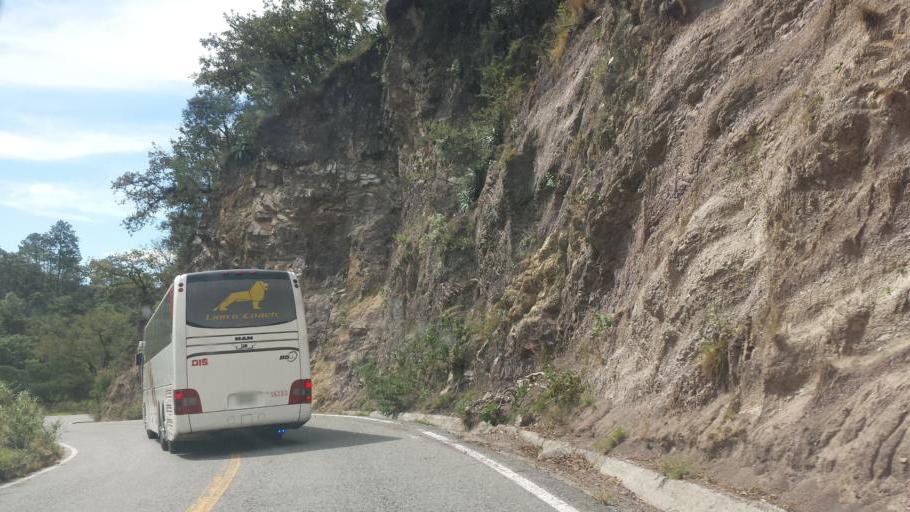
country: MX
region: Oaxaca
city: San Francisco Sola
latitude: 16.4483
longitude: -97.0318
